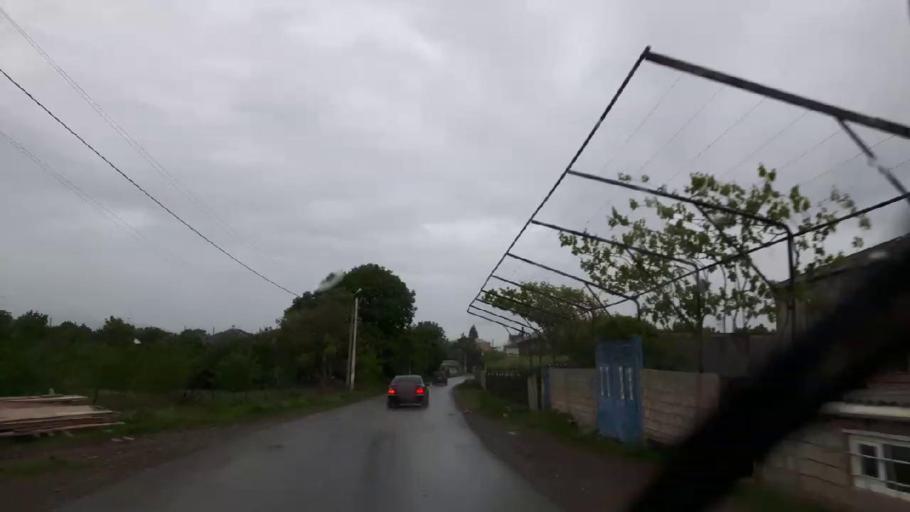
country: GE
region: Shida Kartli
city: Gori
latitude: 41.9912
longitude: 44.0119
